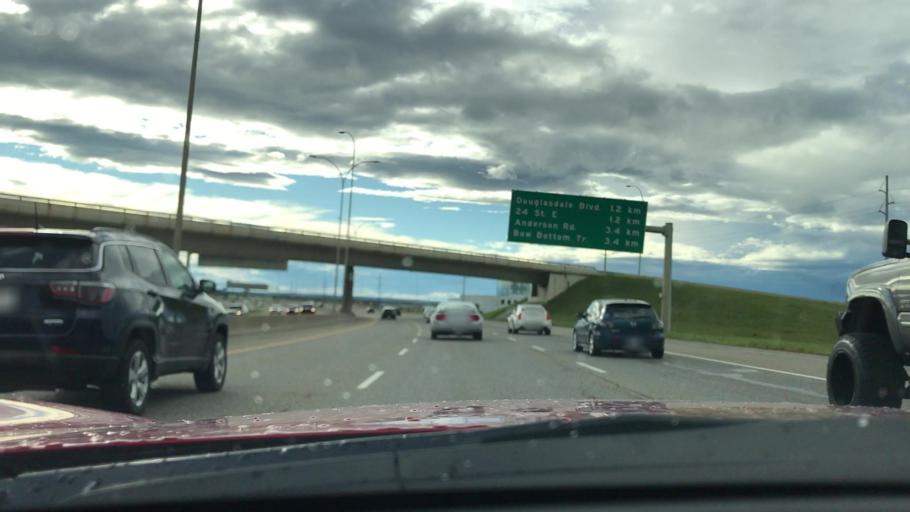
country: CA
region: Alberta
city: Calgary
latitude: 50.9443
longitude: -113.9809
